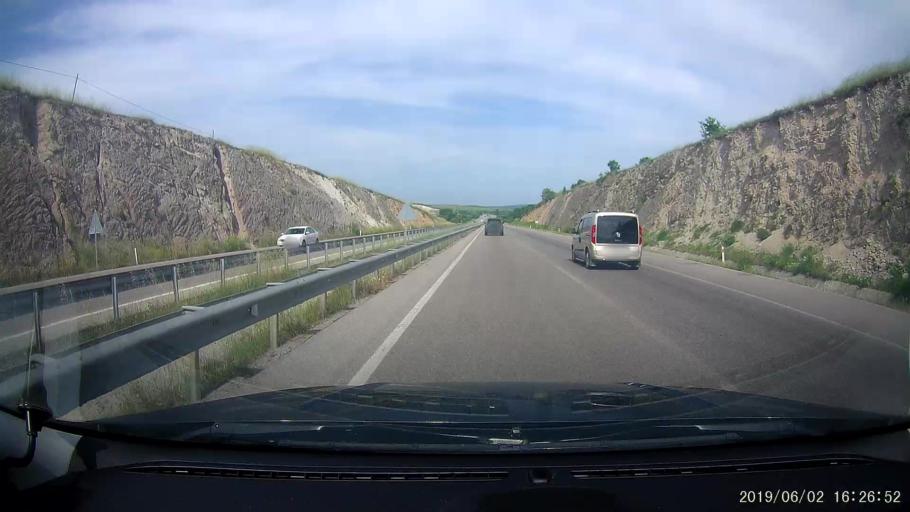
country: TR
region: Samsun
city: Ladik
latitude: 41.0018
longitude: 35.8138
